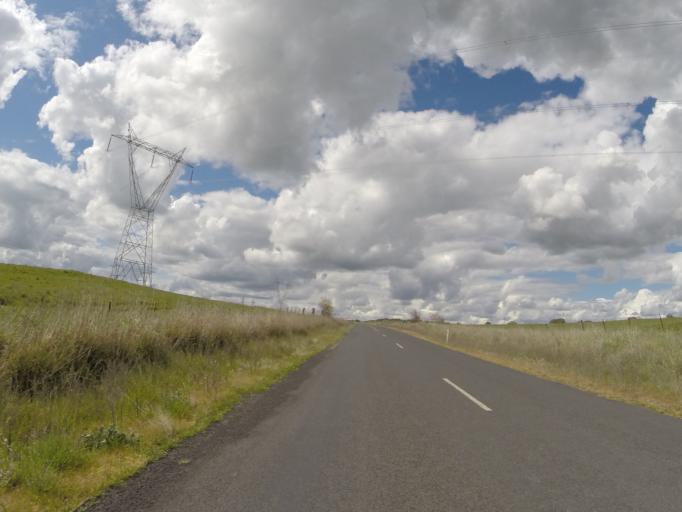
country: AU
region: New South Wales
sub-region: Yass Valley
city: Yass
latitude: -34.8753
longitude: 148.9046
